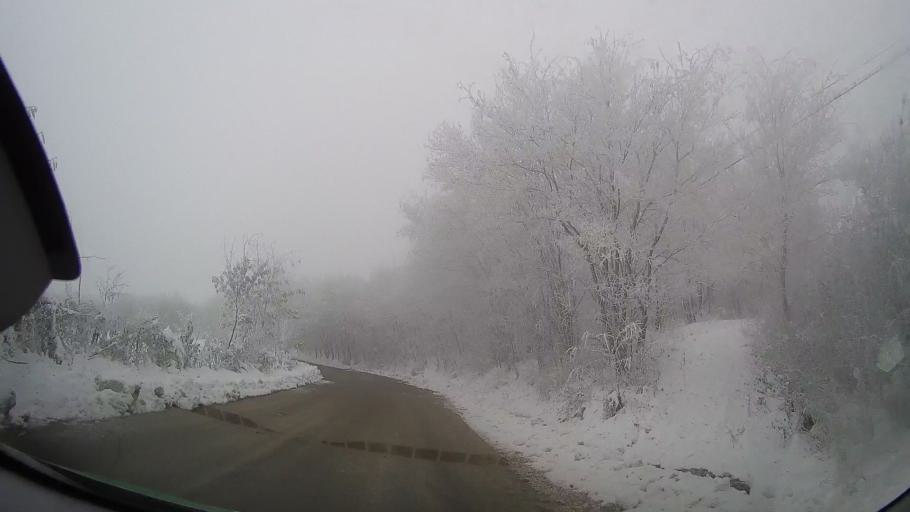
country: RO
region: Iasi
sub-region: Comuna Tansa
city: Suhulet
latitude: 46.8982
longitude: 27.2464
